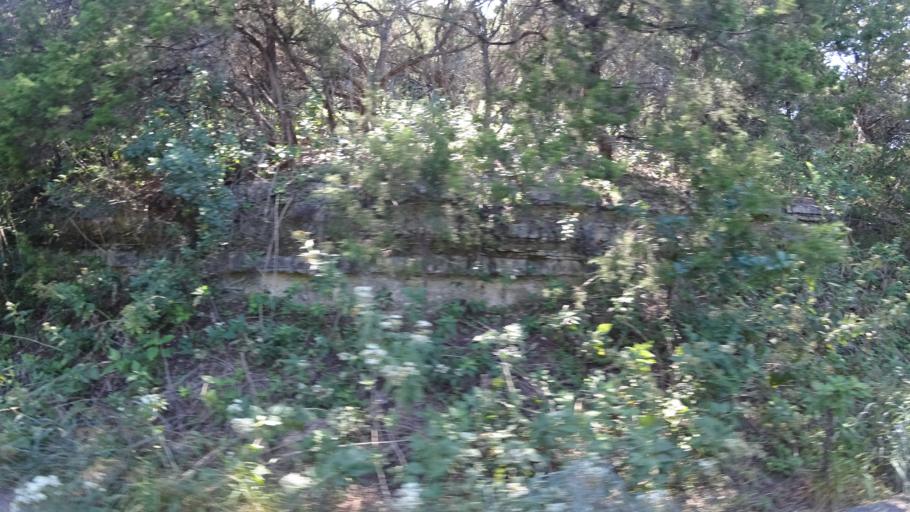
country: US
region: Texas
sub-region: Travis County
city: West Lake Hills
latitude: 30.3050
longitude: -97.8055
